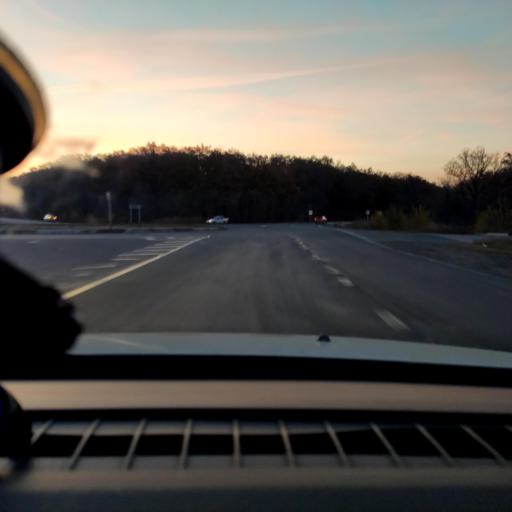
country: RU
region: Samara
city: Novokuybyshevsk
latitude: 52.9834
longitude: 49.8790
